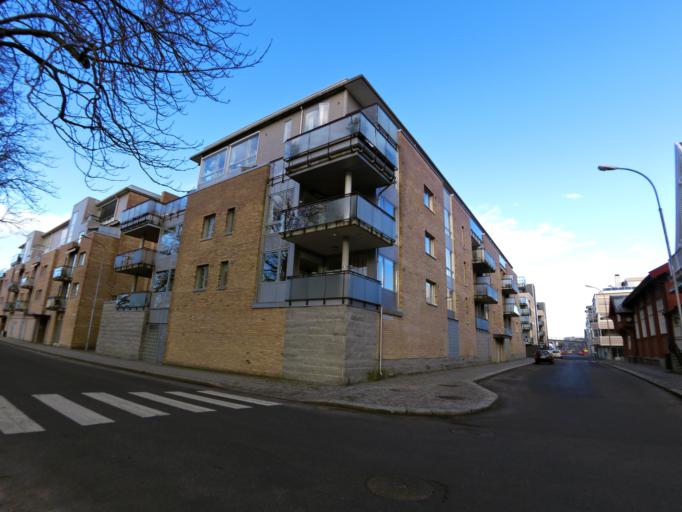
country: NO
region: Ostfold
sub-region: Fredrikstad
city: Fredrikstad
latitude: 59.2067
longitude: 10.9417
